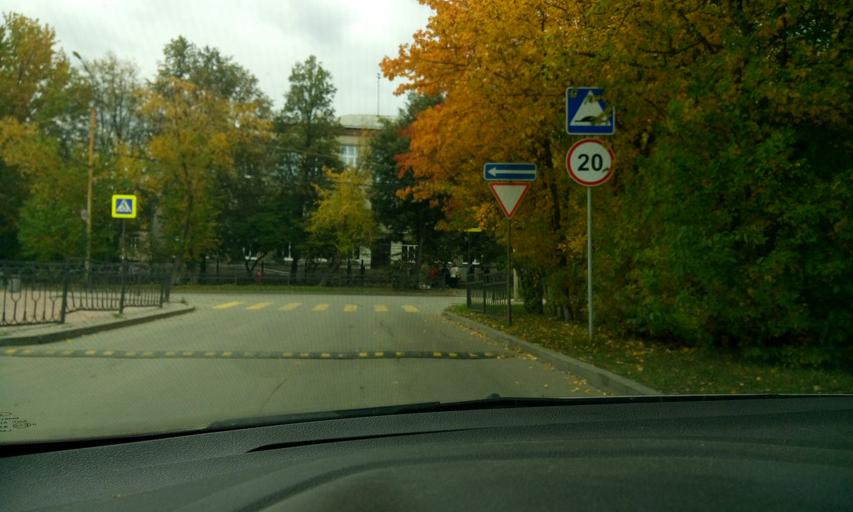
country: RU
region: Sverdlovsk
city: Yekaterinburg
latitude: 56.8509
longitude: 60.6530
